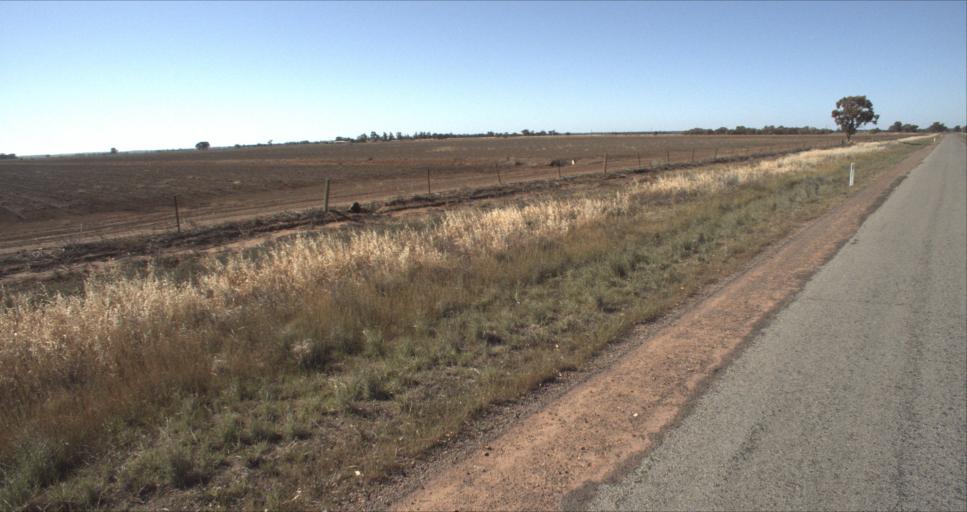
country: AU
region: New South Wales
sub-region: Leeton
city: Leeton
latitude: -34.5615
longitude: 146.3126
